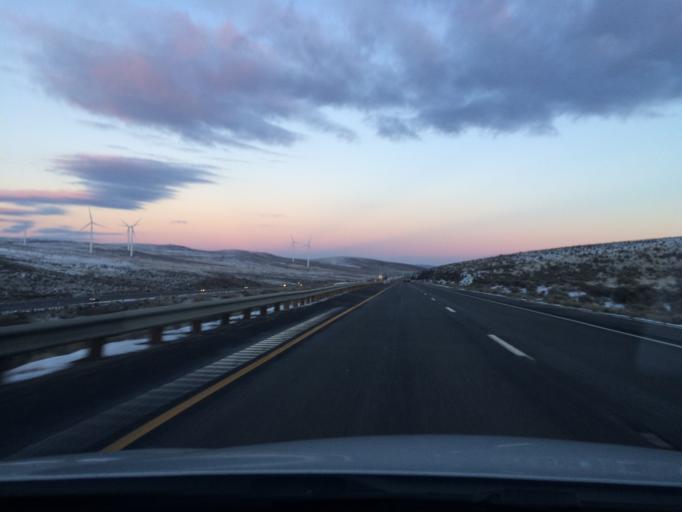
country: US
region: Washington
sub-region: Kittitas County
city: Kittitas
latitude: 46.9397
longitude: -120.1222
